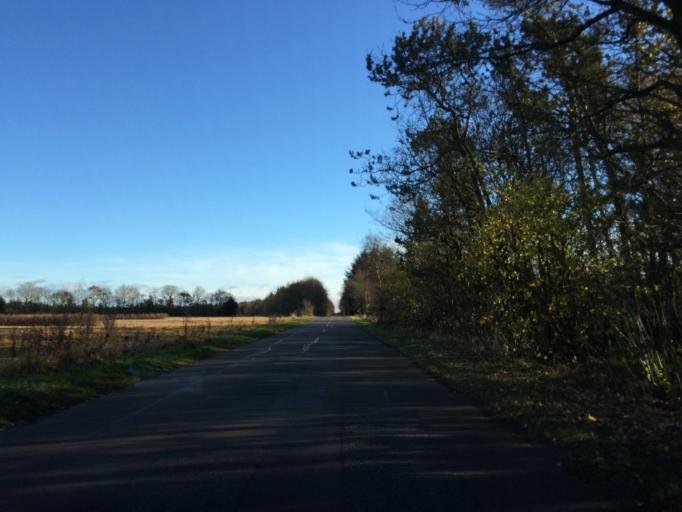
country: DK
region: Central Jutland
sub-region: Ringkobing-Skjern Kommune
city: Videbaek
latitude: 56.0784
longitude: 8.7238
